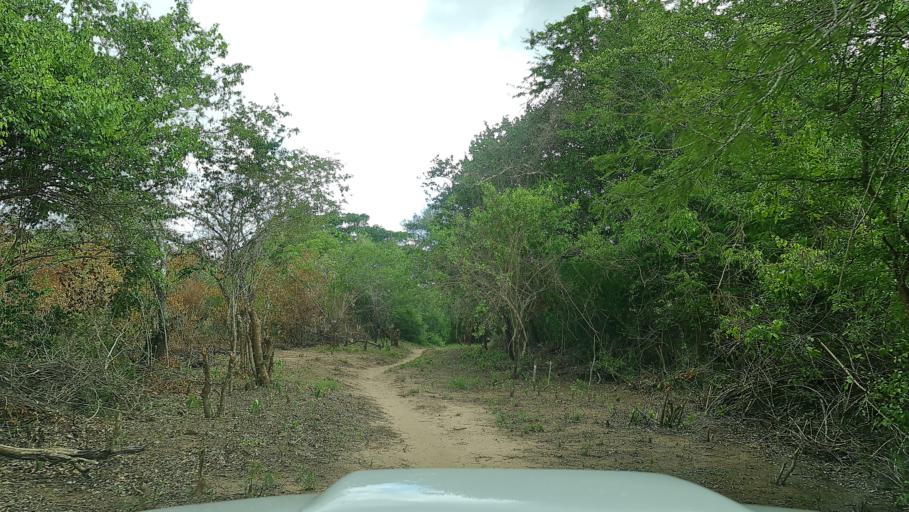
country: MZ
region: Nampula
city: Ilha de Mocambique
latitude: -15.5022
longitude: 40.1580
